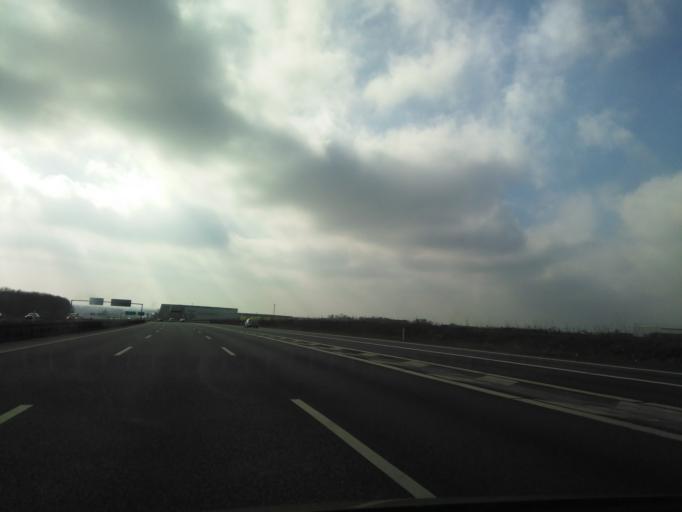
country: DK
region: South Denmark
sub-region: Vejle Kommune
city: Vejle
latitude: 55.7381
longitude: 9.5777
